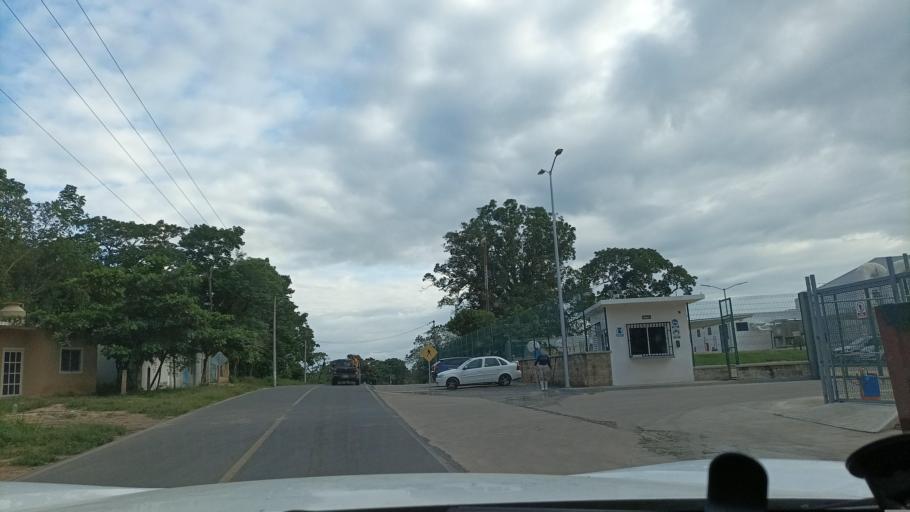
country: MX
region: Veracruz
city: Oluta
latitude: 17.9219
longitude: -94.8879
